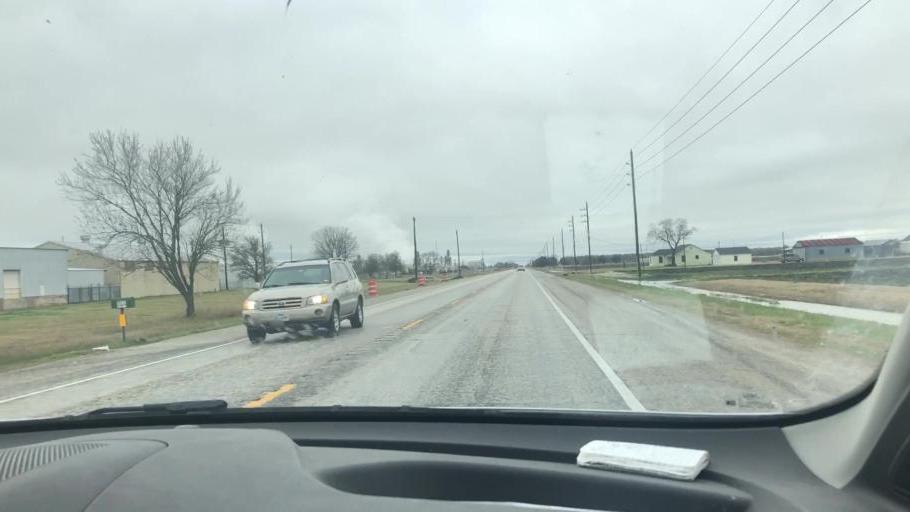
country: US
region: Texas
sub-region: Wharton County
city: Wharton
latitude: 29.2988
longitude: -96.0773
